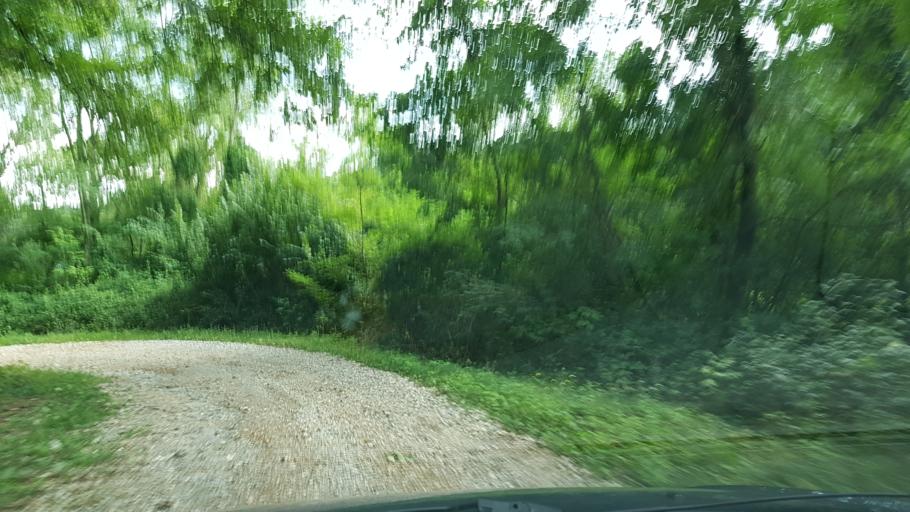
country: SI
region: Kanal
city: Deskle
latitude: 46.0525
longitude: 13.5866
